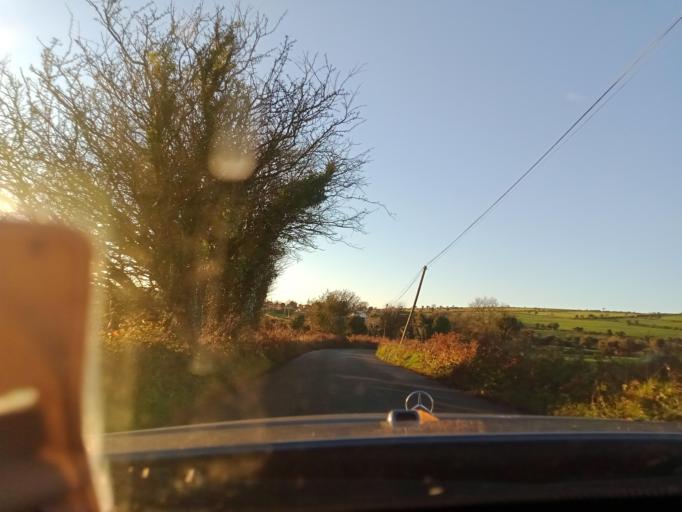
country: IE
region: Leinster
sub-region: Loch Garman
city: New Ross
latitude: 52.3708
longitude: -7.0420
